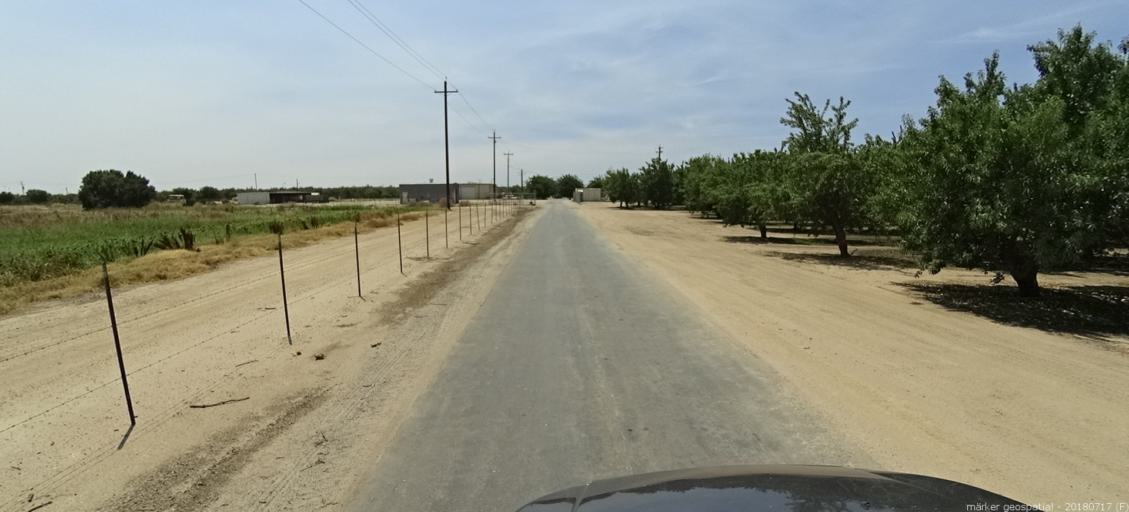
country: US
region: California
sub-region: Madera County
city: Fairmead
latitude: 37.1003
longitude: -120.1659
